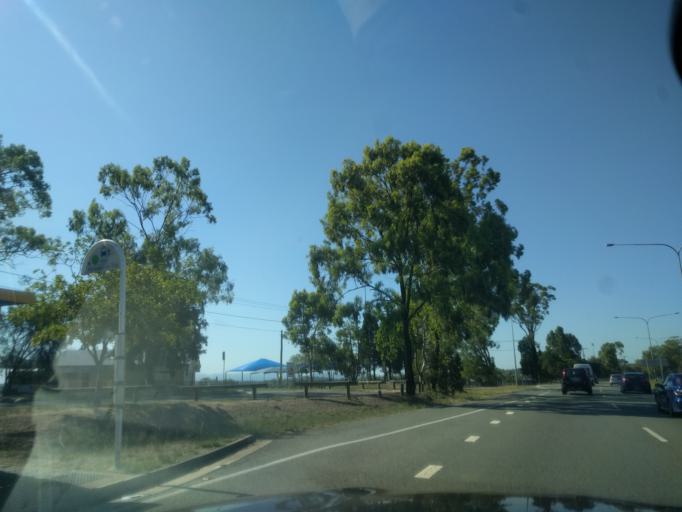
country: AU
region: Queensland
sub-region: Brisbane
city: Sunnybank Hills
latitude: -27.6292
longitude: 153.0463
